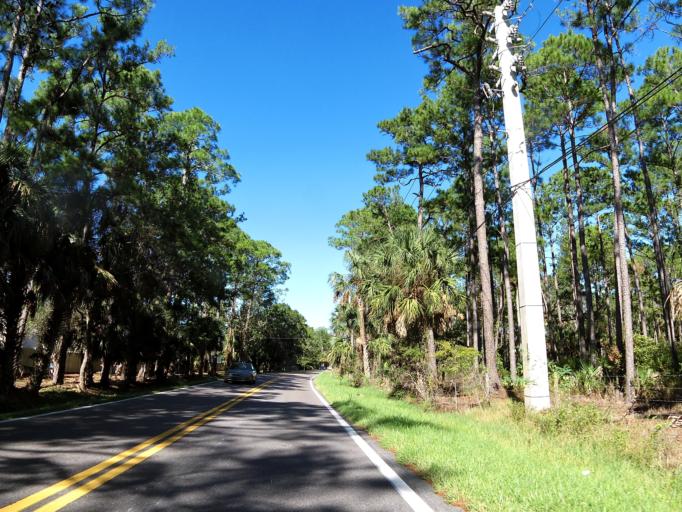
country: US
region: Florida
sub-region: Saint Johns County
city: Palm Valley
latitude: 30.1393
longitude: -81.3796
